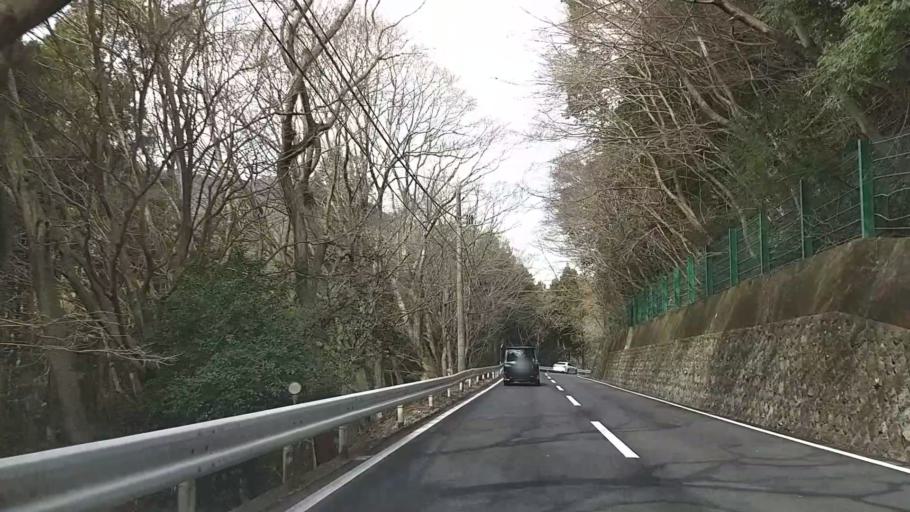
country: JP
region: Shizuoka
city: Heda
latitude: 34.8480
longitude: 138.9217
